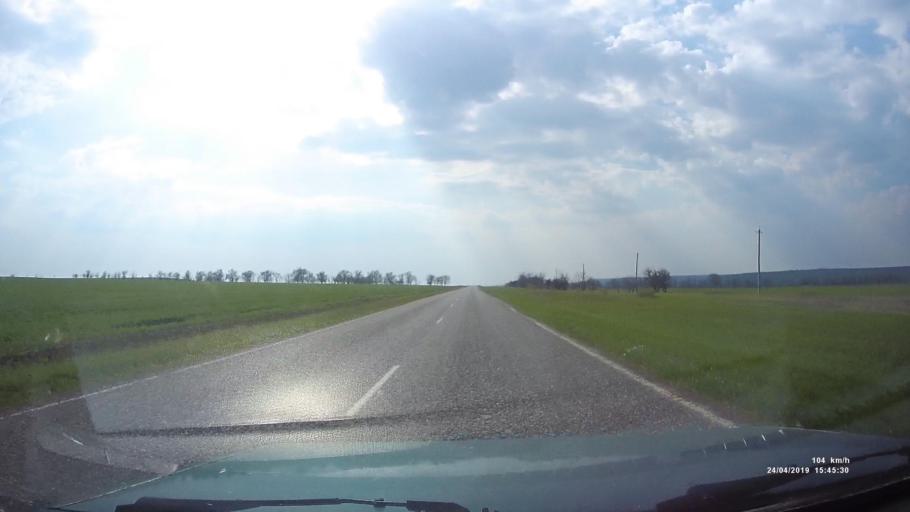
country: RU
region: Kalmykiya
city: Yashalta
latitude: 46.5918
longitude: 42.7364
